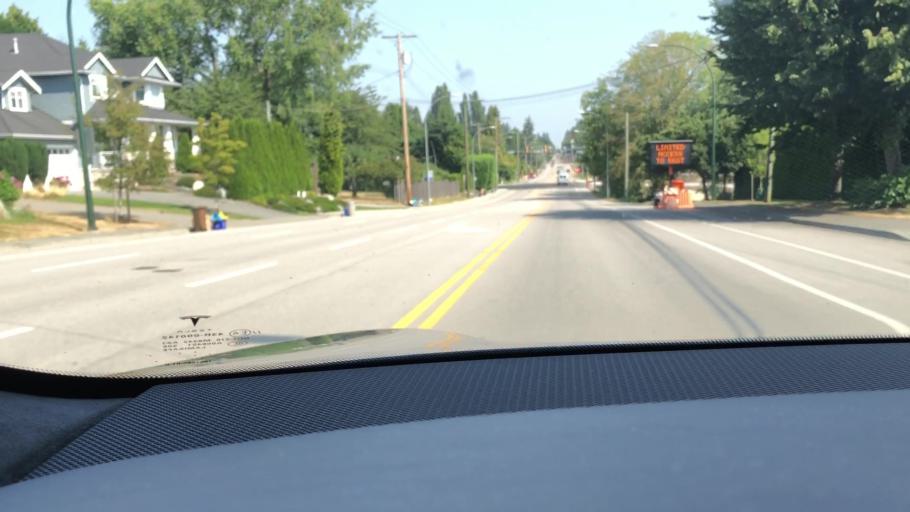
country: US
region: Washington
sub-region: Whatcom County
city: Point Roberts
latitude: 49.0086
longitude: -123.0686
